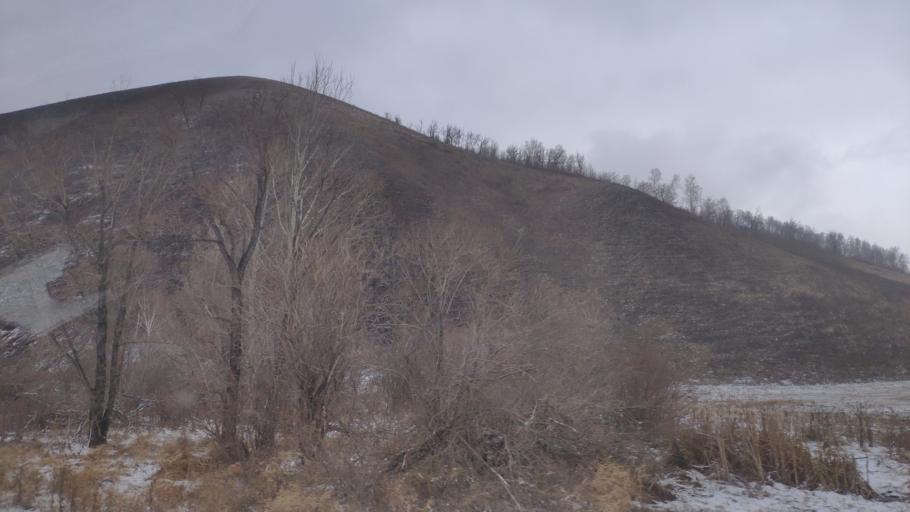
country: RU
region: Bashkortostan
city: Isyangulovo
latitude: 52.1609
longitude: 56.9195
